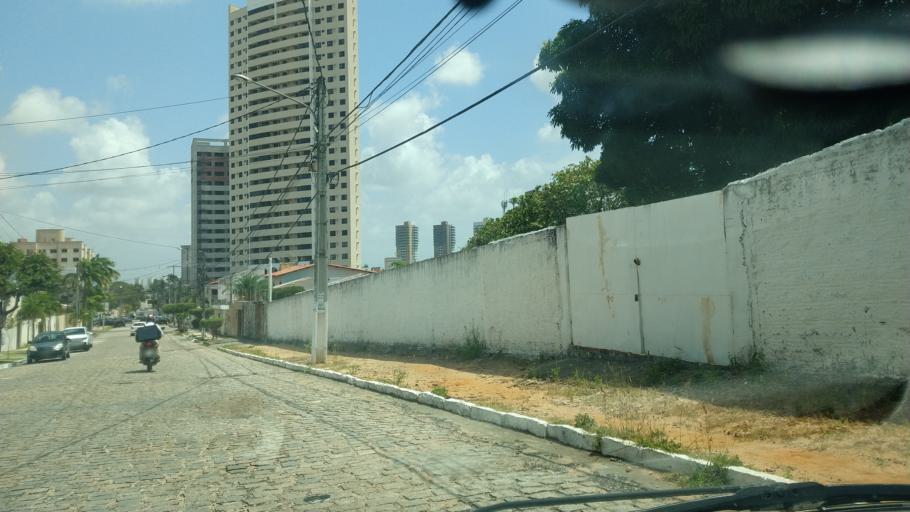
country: BR
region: Rio Grande do Norte
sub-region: Natal
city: Natal
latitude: -5.8608
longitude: -35.1941
